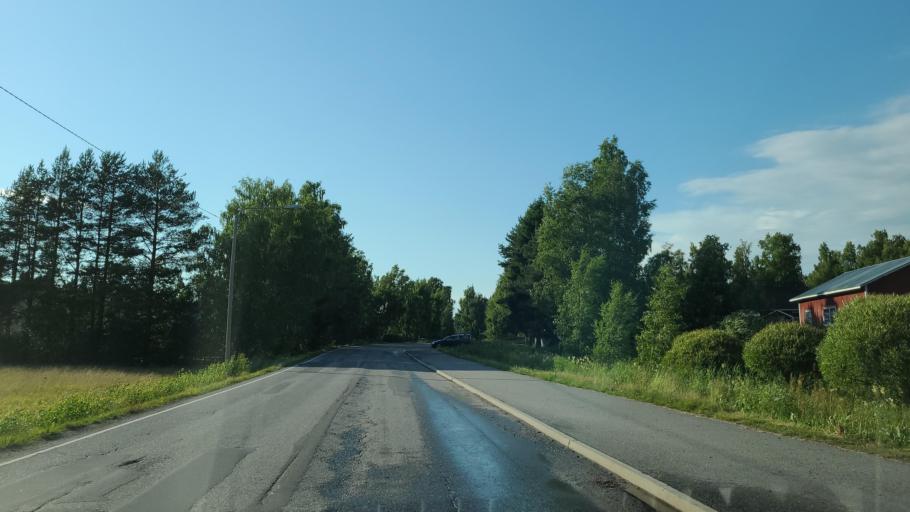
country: FI
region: Ostrobothnia
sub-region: Vaasa
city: Replot
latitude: 63.2220
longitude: 21.4135
